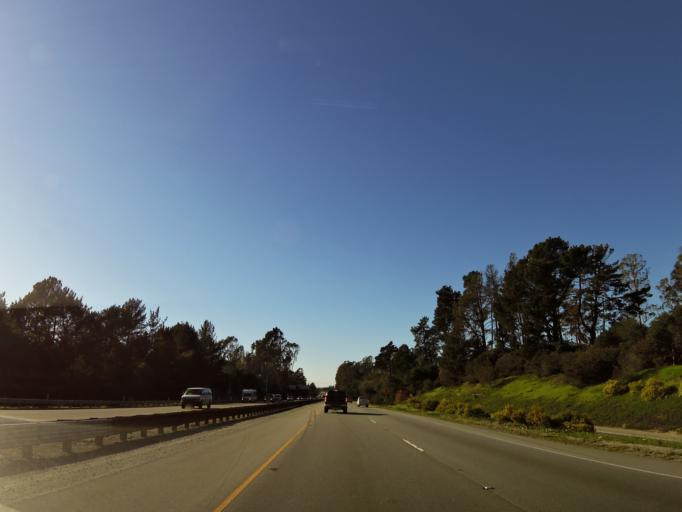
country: US
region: California
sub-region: Santa Cruz County
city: Capitola
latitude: 36.9841
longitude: -121.9380
